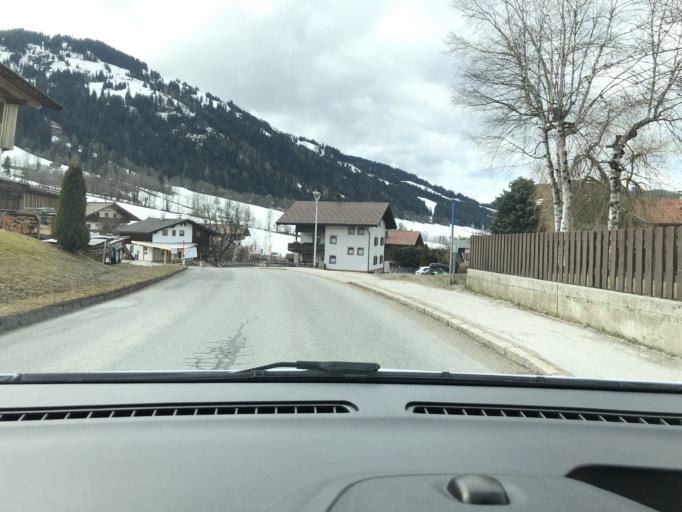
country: AT
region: Tyrol
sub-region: Politischer Bezirk Kitzbuhel
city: Itter
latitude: 47.4484
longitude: 12.1036
